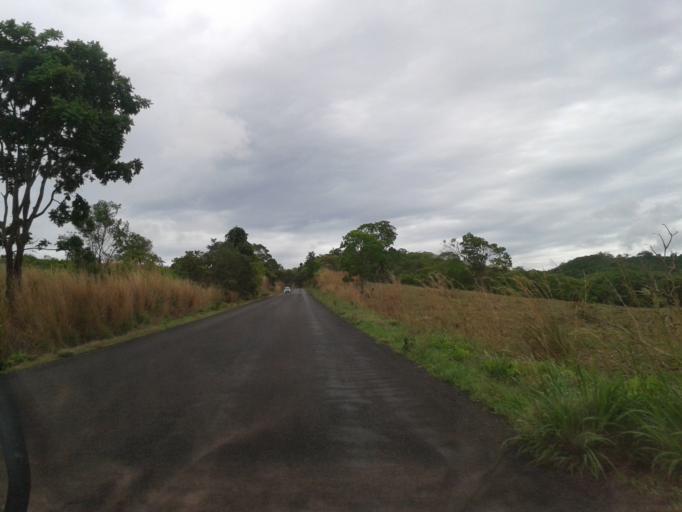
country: BR
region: Goias
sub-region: Buriti Alegre
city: Buriti Alegre
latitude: -18.0583
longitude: -48.7328
